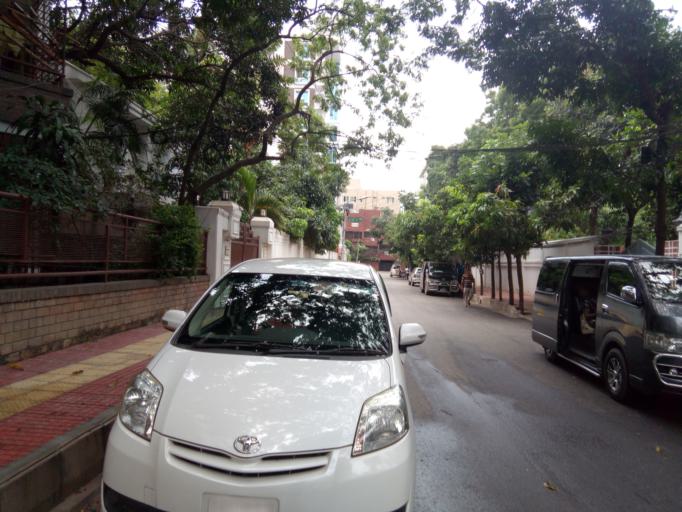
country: BD
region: Dhaka
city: Paltan
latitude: 23.7936
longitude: 90.4121
